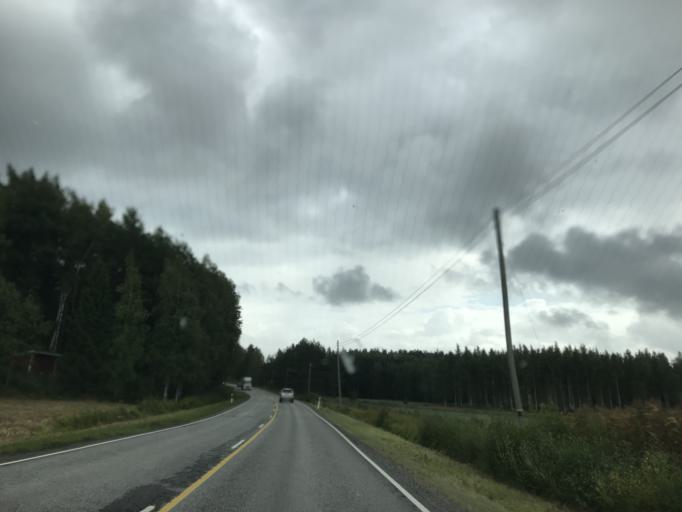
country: FI
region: Varsinais-Suomi
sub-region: Salo
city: Pernioe
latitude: 60.0855
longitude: 23.2307
